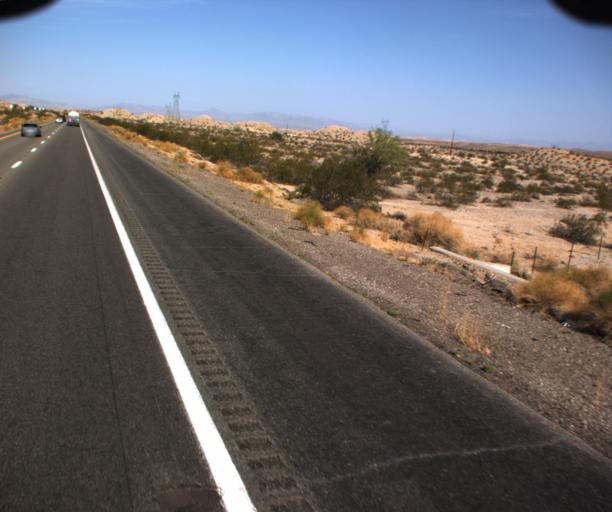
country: US
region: Arizona
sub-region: Mohave County
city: Desert Hills
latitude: 34.7277
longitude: -114.3791
